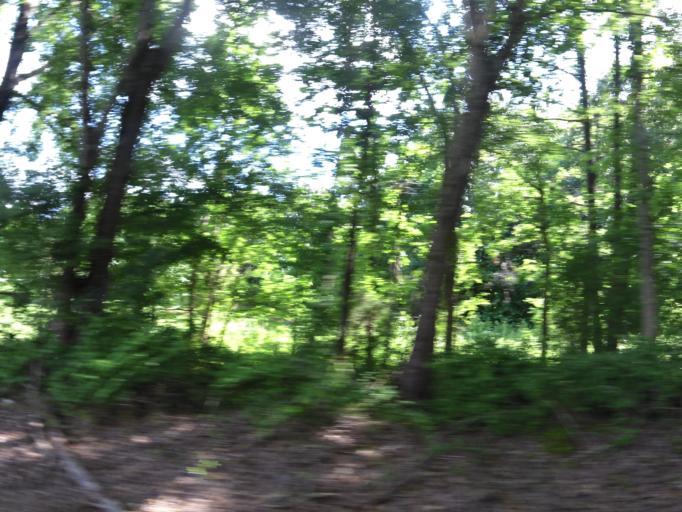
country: US
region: Tennessee
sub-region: Gibson County
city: Milan
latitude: 35.9771
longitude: -88.7227
